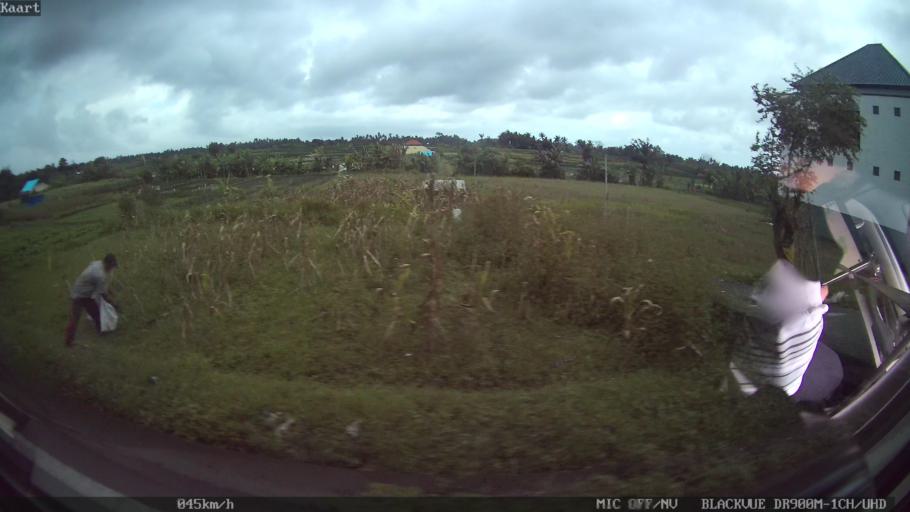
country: ID
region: Bali
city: Banjar Mambalkajanan
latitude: -8.5444
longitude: 115.2223
